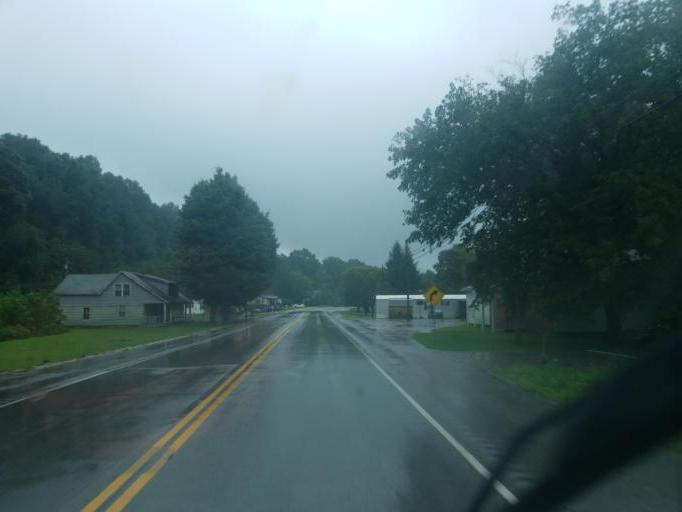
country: US
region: Kentucky
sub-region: Rowan County
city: Morehead
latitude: 38.2495
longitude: -83.3419
